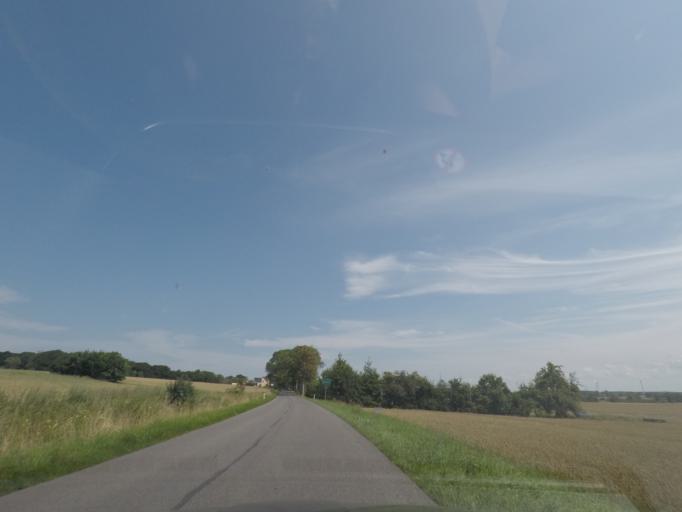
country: PL
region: West Pomeranian Voivodeship
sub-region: Powiat slawienski
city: Darlowo
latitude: 54.4673
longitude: 16.5516
